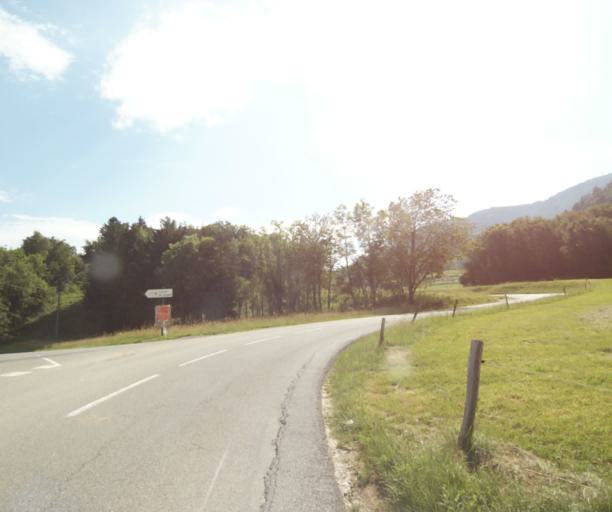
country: FR
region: Rhone-Alpes
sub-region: Departement de la Haute-Savoie
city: Armoy
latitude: 46.3361
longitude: 6.5103
